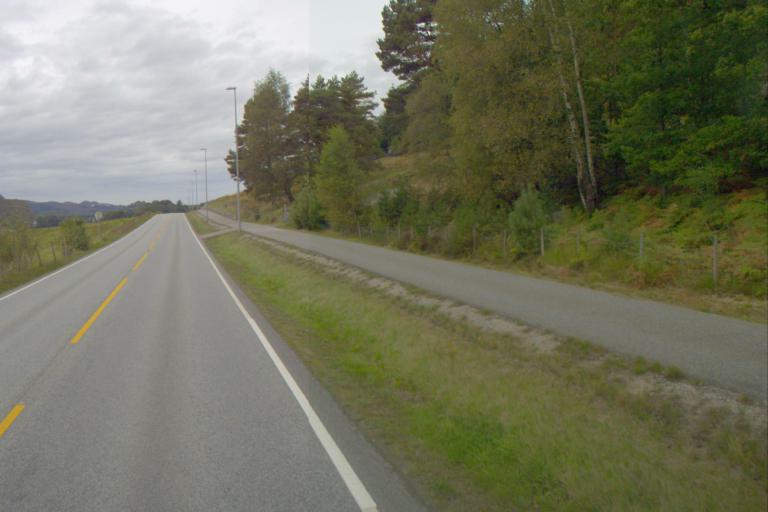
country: NO
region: Rogaland
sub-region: Sandnes
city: Hommersak
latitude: 58.8769
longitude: 5.8256
